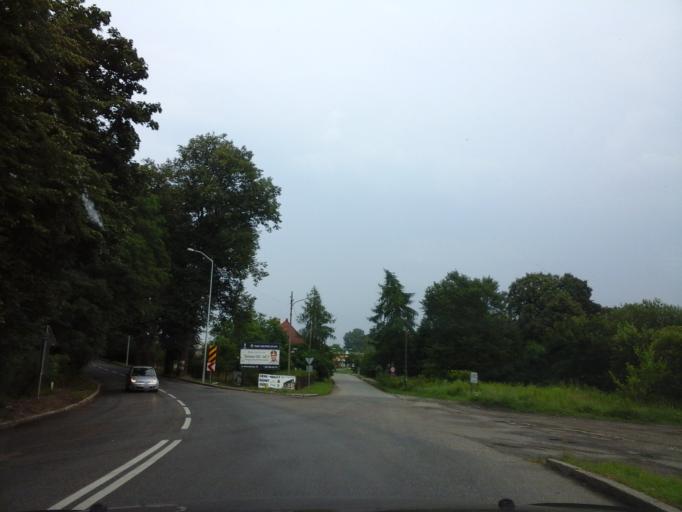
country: PL
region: Lubusz
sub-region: Powiat strzelecko-drezdenecki
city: Drezdenko
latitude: 52.8536
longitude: 15.8301
